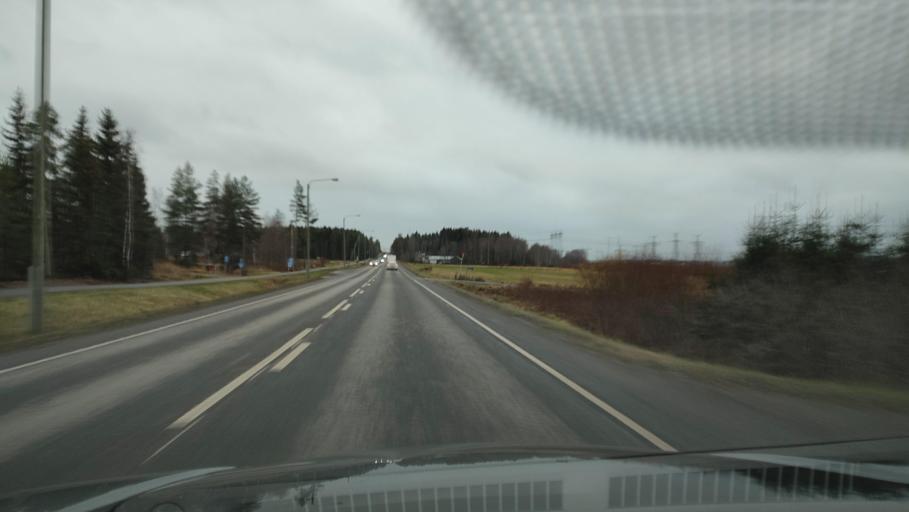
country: FI
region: Southern Ostrobothnia
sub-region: Seinaejoki
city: Seinaejoki
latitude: 62.7894
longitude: 22.7271
